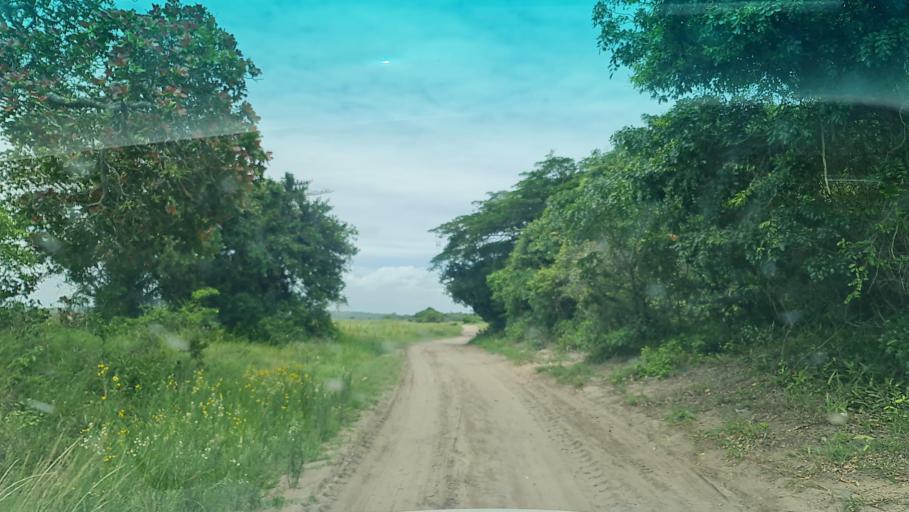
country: MZ
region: Maputo
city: Manhica
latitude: -25.5278
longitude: 32.8515
